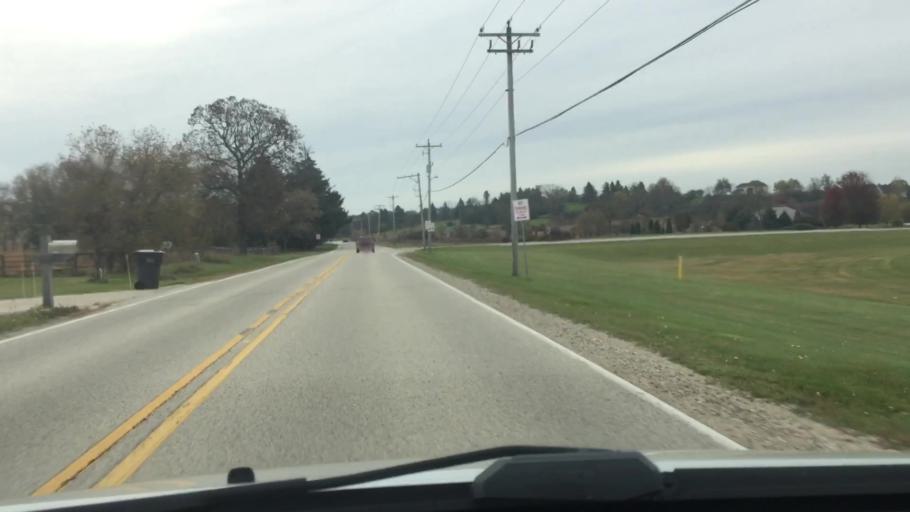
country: US
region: Wisconsin
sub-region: Waukesha County
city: Mukwonago
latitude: 42.8877
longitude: -88.3774
